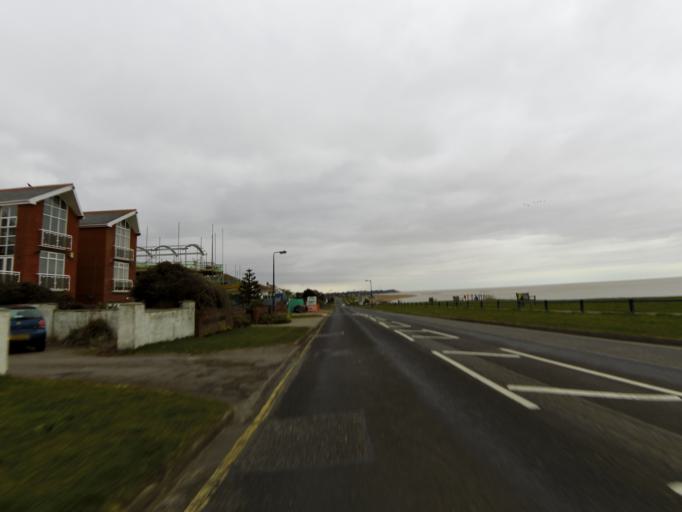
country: GB
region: England
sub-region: Suffolk
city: Felixstowe
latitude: 51.9715
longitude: 1.3761
